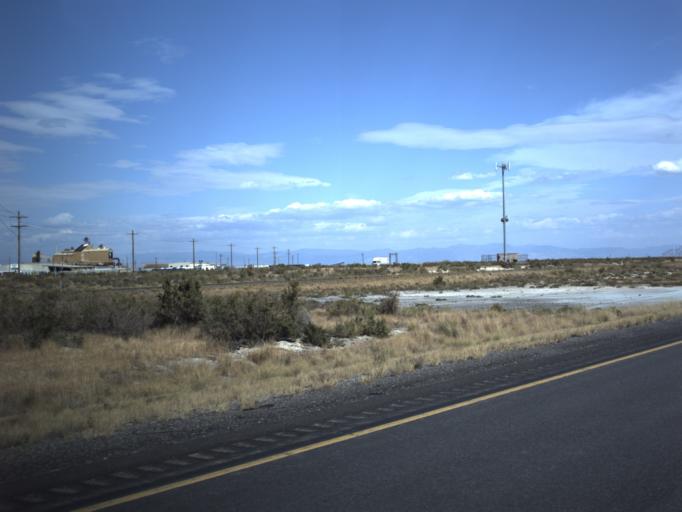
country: US
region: Utah
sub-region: Tooele County
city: Grantsville
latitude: 40.7053
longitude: -112.5162
